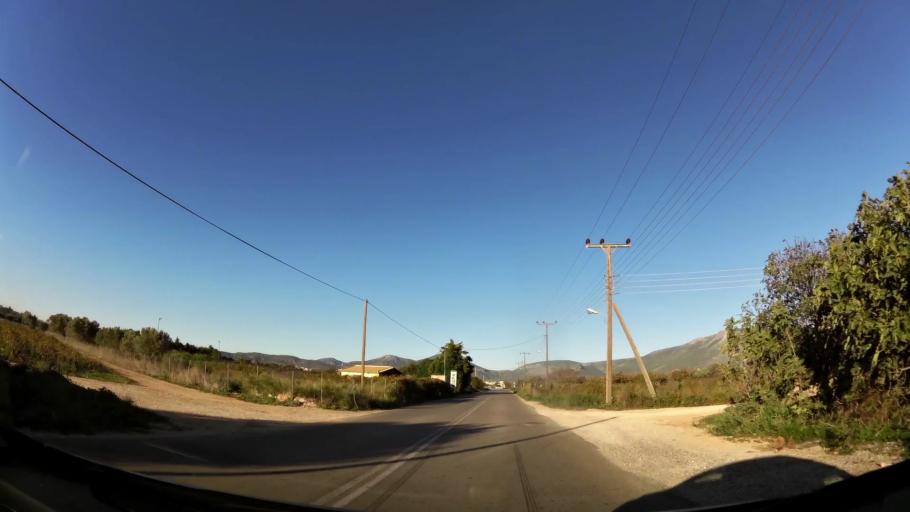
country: GR
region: Attica
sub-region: Nomarchia Anatolikis Attikis
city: Koropi
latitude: 37.9144
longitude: 23.9031
